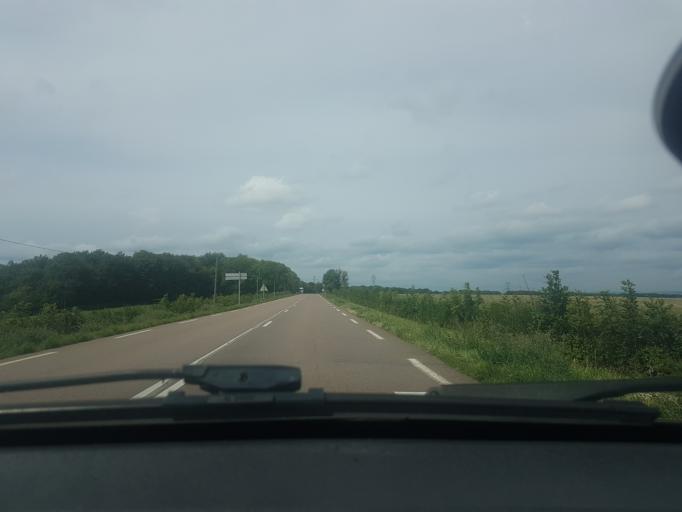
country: FR
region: Bourgogne
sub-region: Departement de la Cote-d'Or
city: Nolay
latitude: 47.0370
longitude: 4.6242
